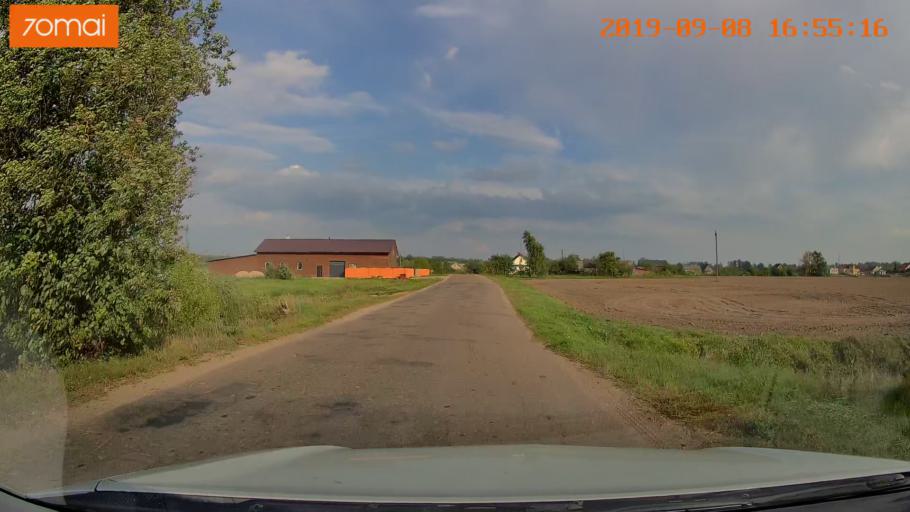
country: BY
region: Grodnenskaya
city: Hrodna
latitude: 53.7485
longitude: 23.9310
